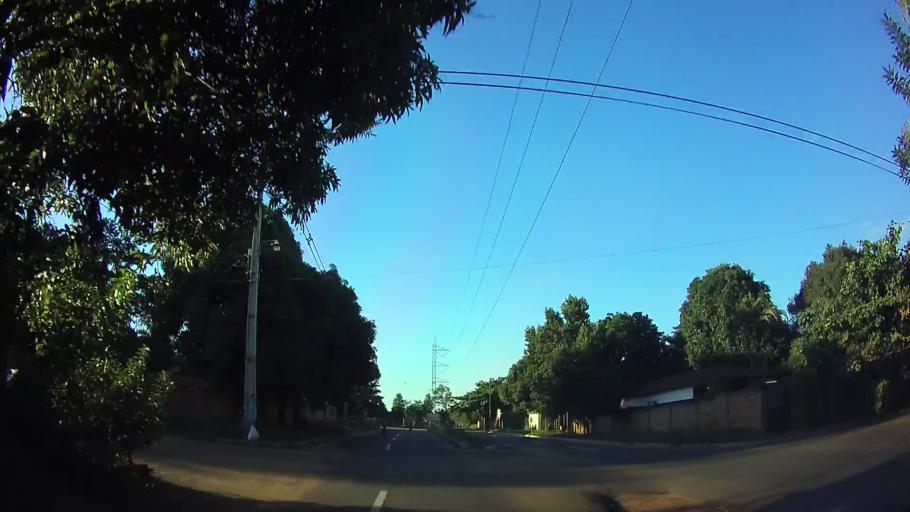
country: PY
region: Central
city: San Lorenzo
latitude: -25.2775
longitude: -57.4638
